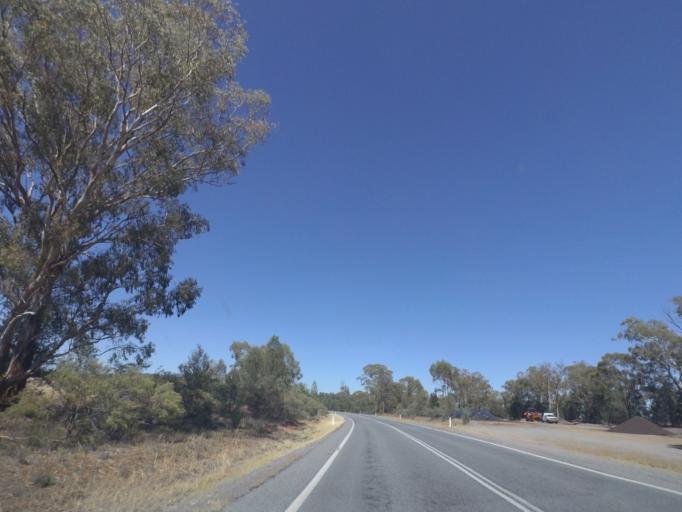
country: AU
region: New South Wales
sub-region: Narrandera
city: Narrandera
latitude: -34.4188
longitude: 146.8491
